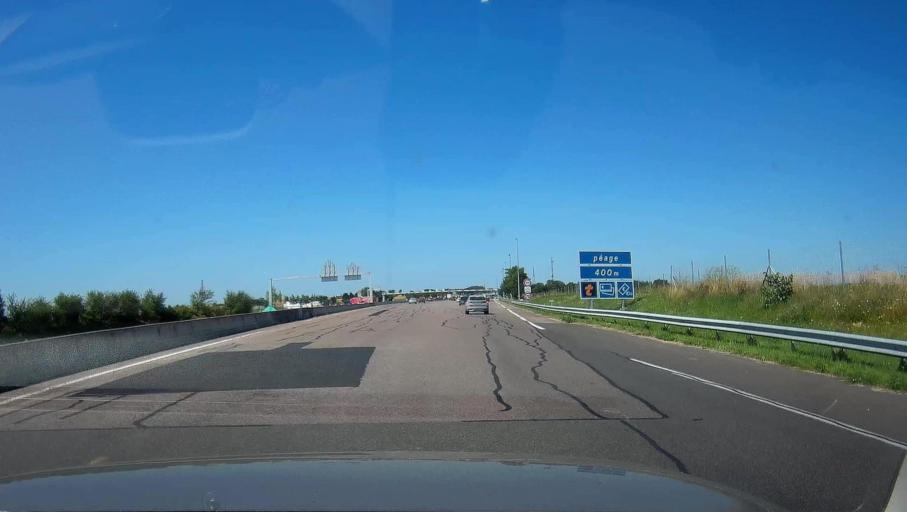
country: FR
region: Champagne-Ardenne
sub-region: Departement de la Marne
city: Taissy
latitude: 49.2086
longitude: 4.0828
